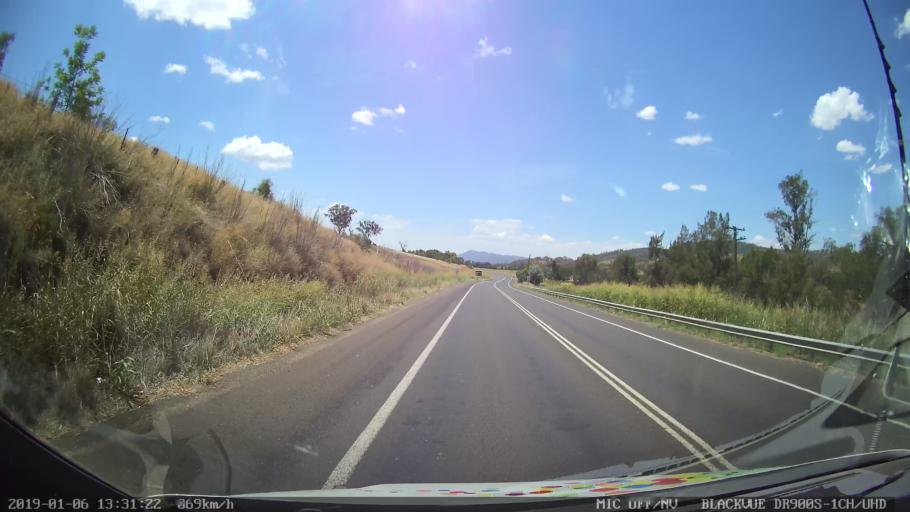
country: AU
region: New South Wales
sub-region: Tamworth Municipality
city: East Tamworth
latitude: -31.1220
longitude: 150.9929
